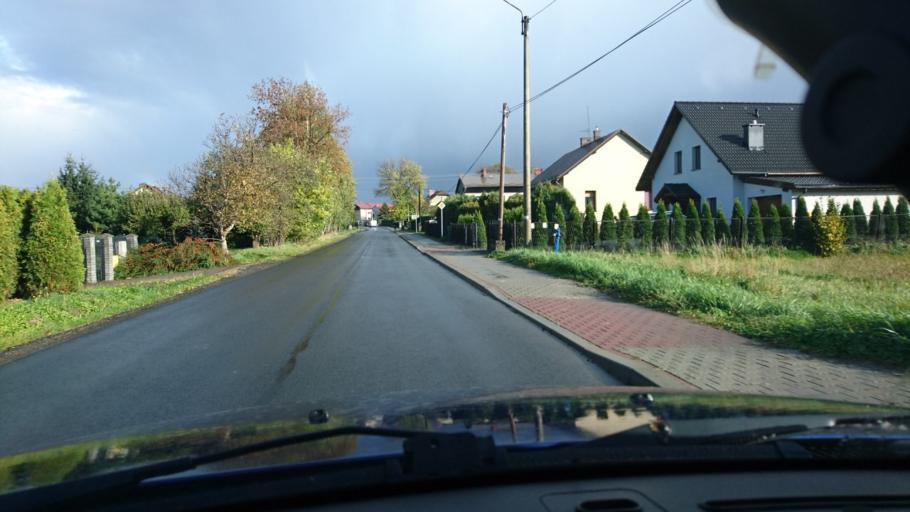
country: PL
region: Silesian Voivodeship
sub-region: Powiat bielski
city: Mazancowice
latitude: 49.8590
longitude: 19.0032
